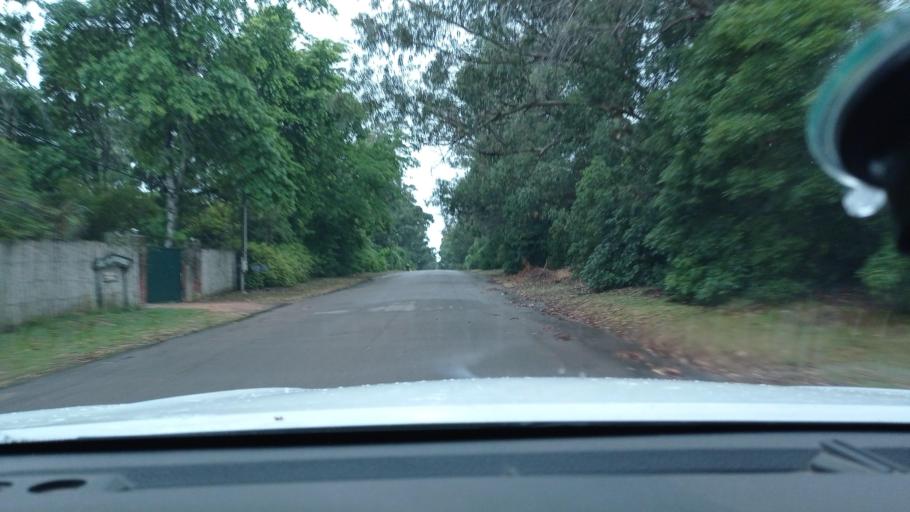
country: UY
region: Maldonado
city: Maldonado
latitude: -34.9177
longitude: -54.9117
